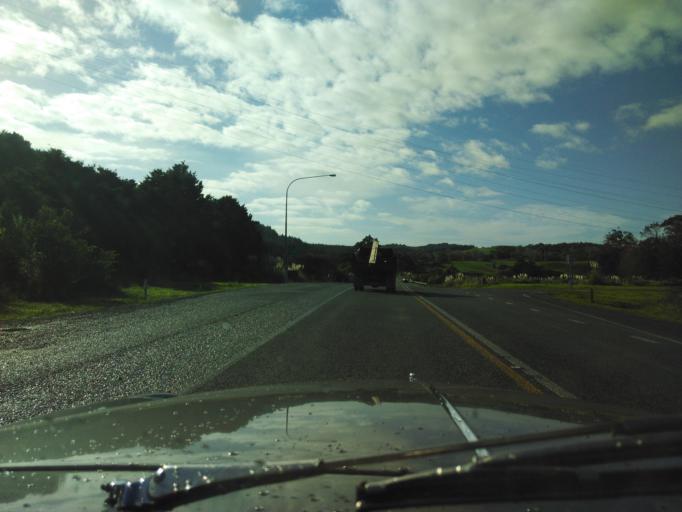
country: NZ
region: Auckland
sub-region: Auckland
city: Wellsford
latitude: -36.2127
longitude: 174.4675
